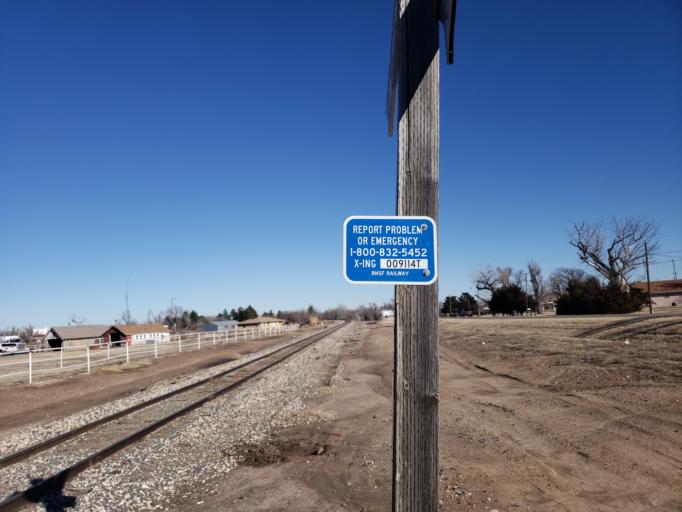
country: US
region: Kansas
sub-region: Ford County
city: Dodge City
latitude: 37.7324
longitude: -100.0407
